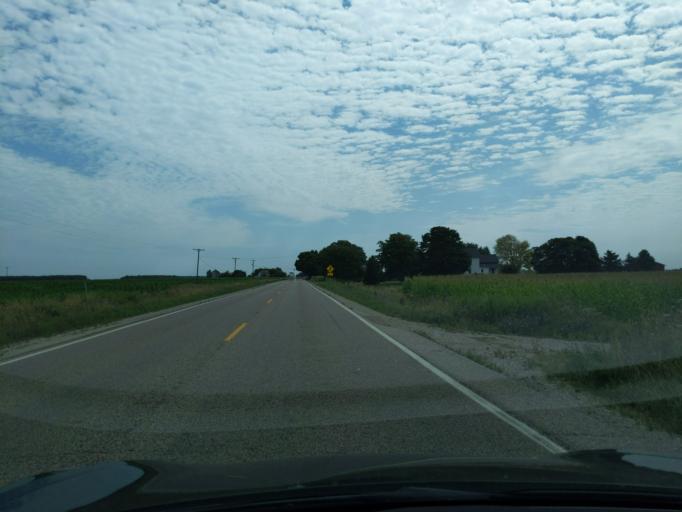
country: US
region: Michigan
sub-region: Gratiot County
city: Ithaca
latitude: 43.2917
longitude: -84.4919
